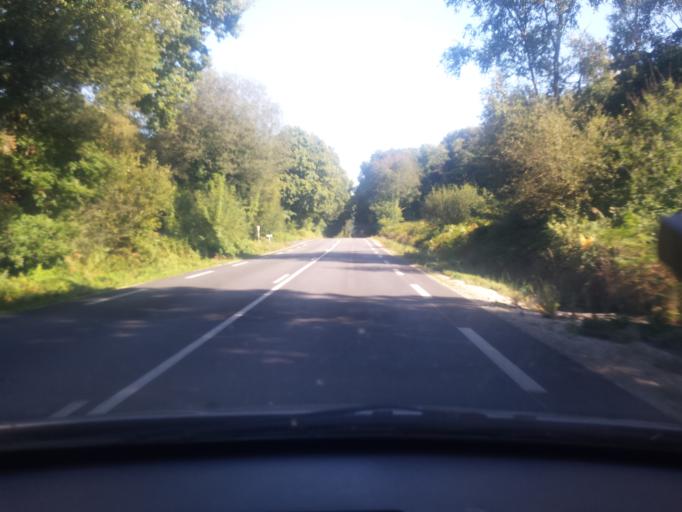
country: FR
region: Brittany
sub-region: Departement du Morbihan
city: Malguenac
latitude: 48.0990
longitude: -3.0578
